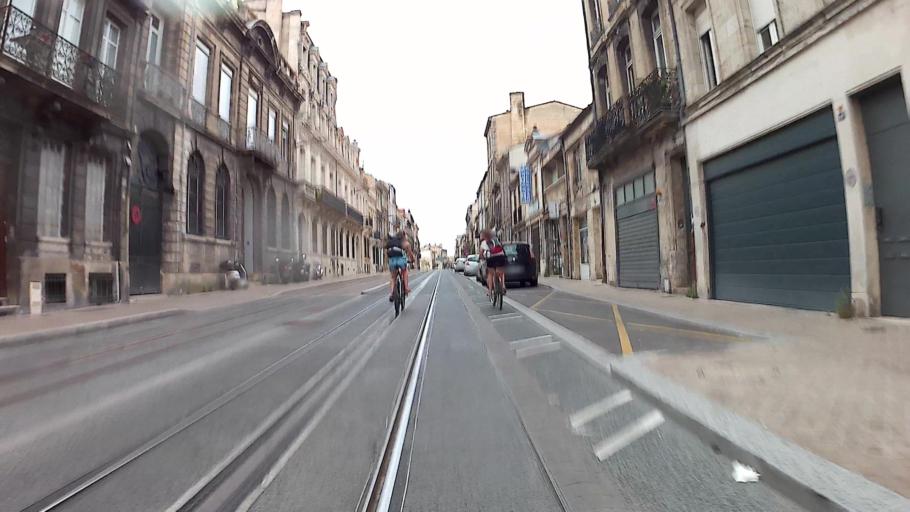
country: FR
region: Aquitaine
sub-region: Departement de la Gironde
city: Bordeaux
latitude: 44.8506
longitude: -0.5875
